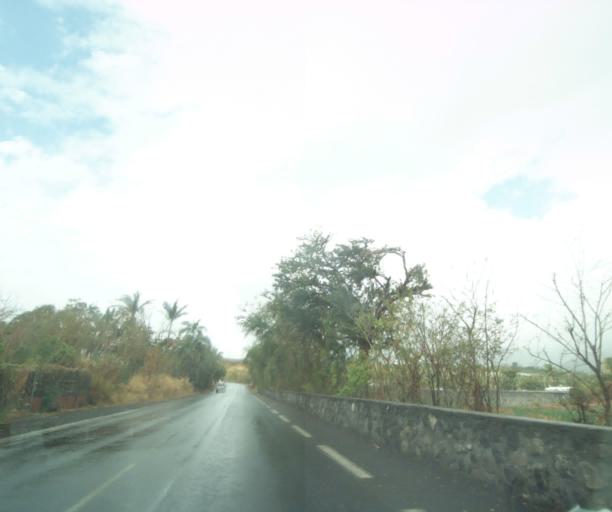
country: RE
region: Reunion
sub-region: Reunion
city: Le Port
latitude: -20.9727
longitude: 55.3070
